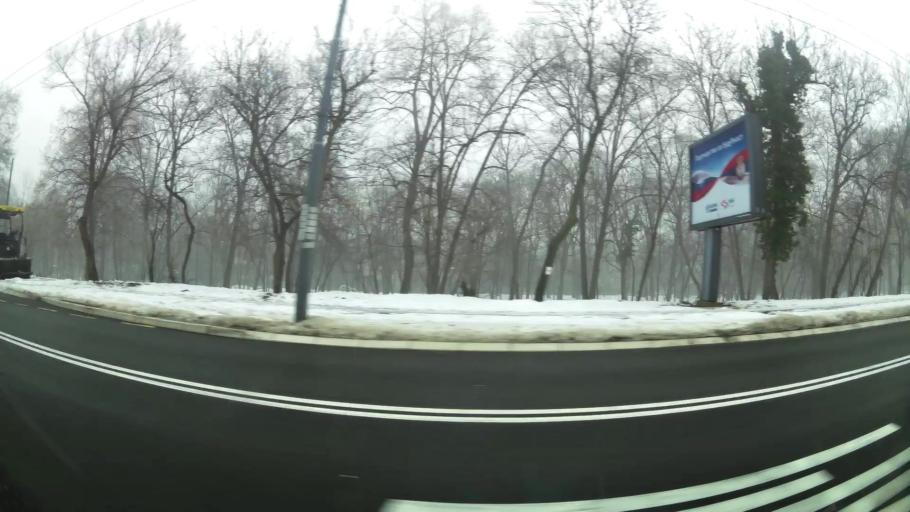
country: RS
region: Central Serbia
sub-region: Belgrade
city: Savski Venac
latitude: 44.7858
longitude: 20.4575
